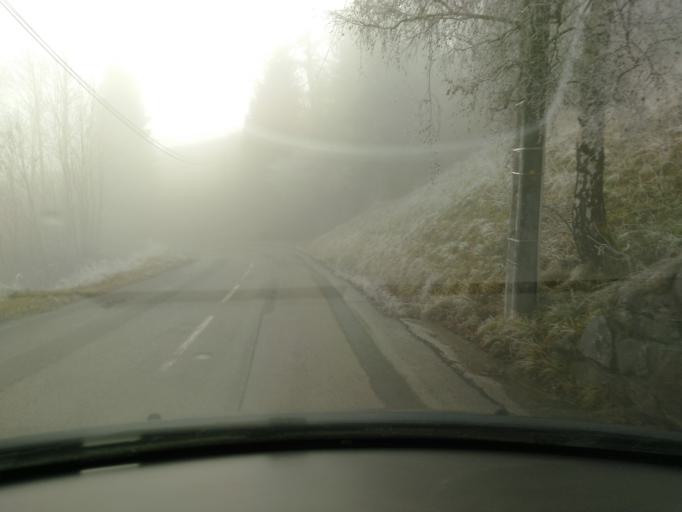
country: FR
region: Rhone-Alpes
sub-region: Departement de la Haute-Savoie
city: Sallanches
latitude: 45.9622
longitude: 6.6176
